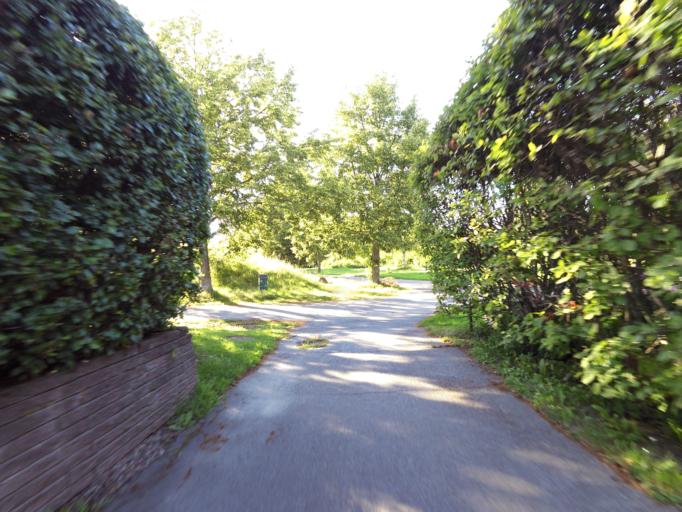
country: SE
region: Gaevleborg
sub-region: Gavle Kommun
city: Gavle
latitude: 60.6491
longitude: 17.1421
